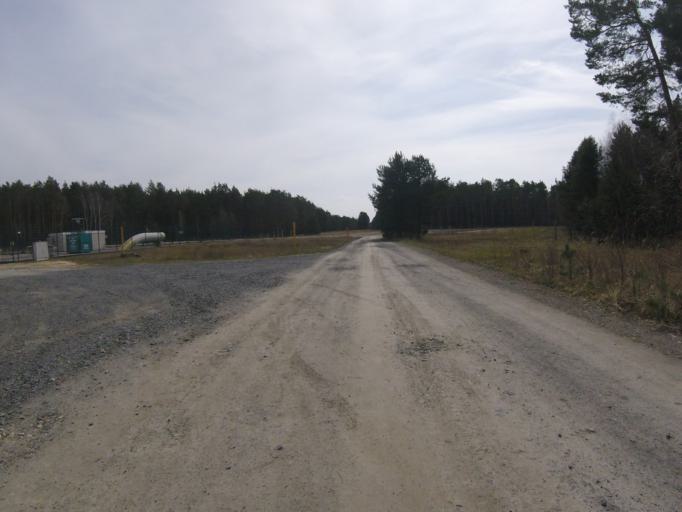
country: DE
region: Brandenburg
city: Schwerin
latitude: 52.1845
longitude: 13.6271
